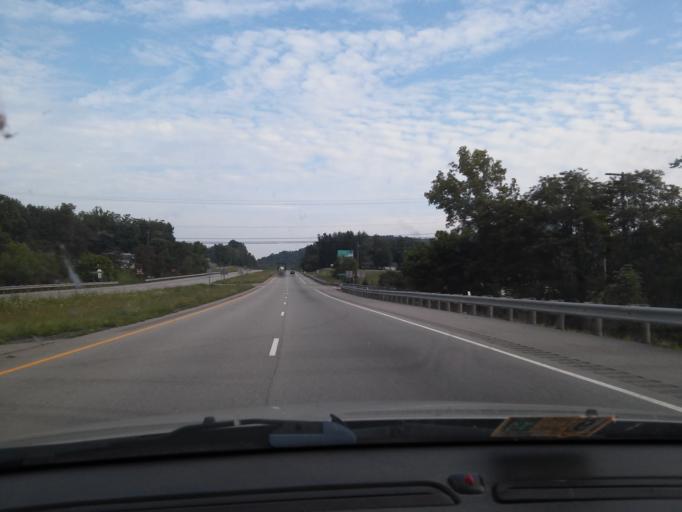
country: US
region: Ohio
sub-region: Jackson County
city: Jackson
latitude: 39.1733
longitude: -82.7468
